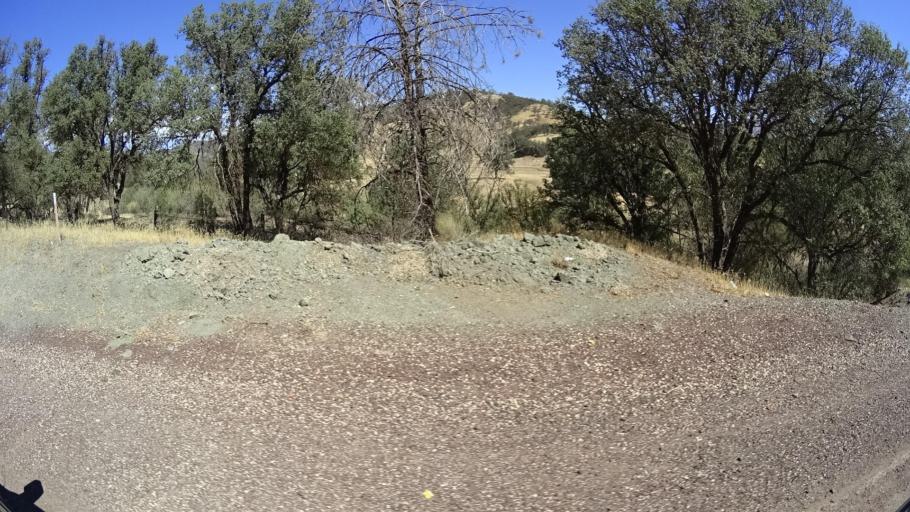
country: US
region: California
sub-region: Fresno County
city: Coalinga
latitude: 36.2015
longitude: -120.7314
